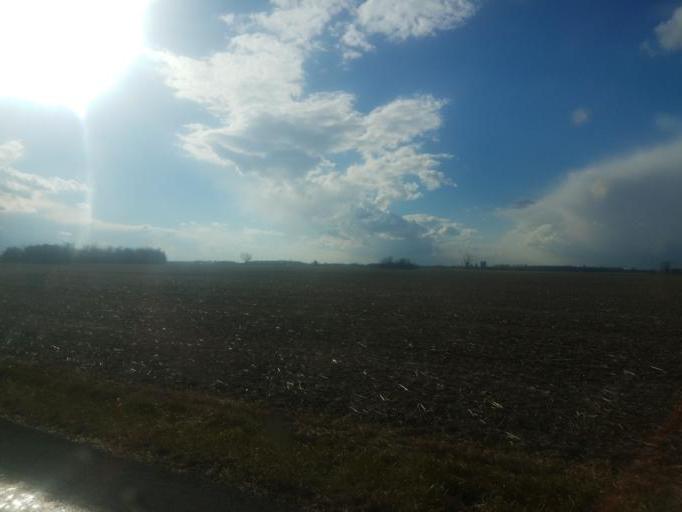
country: US
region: Ohio
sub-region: Marion County
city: Prospect
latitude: 40.4797
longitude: -83.1319
